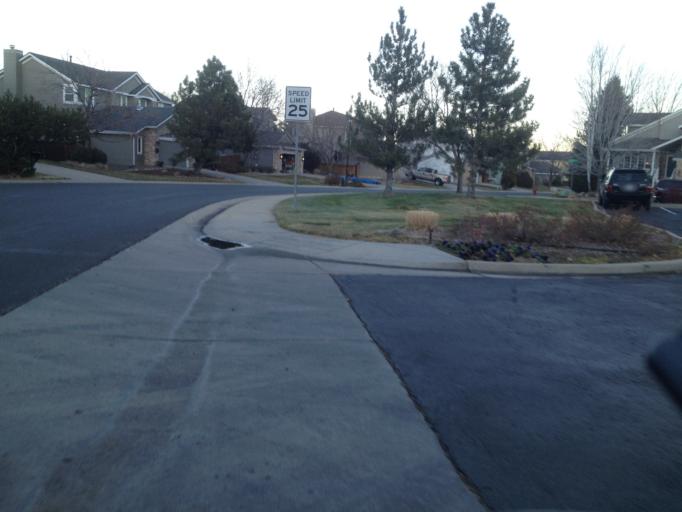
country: US
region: Colorado
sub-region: Boulder County
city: Superior
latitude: 39.9573
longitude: -105.1505
